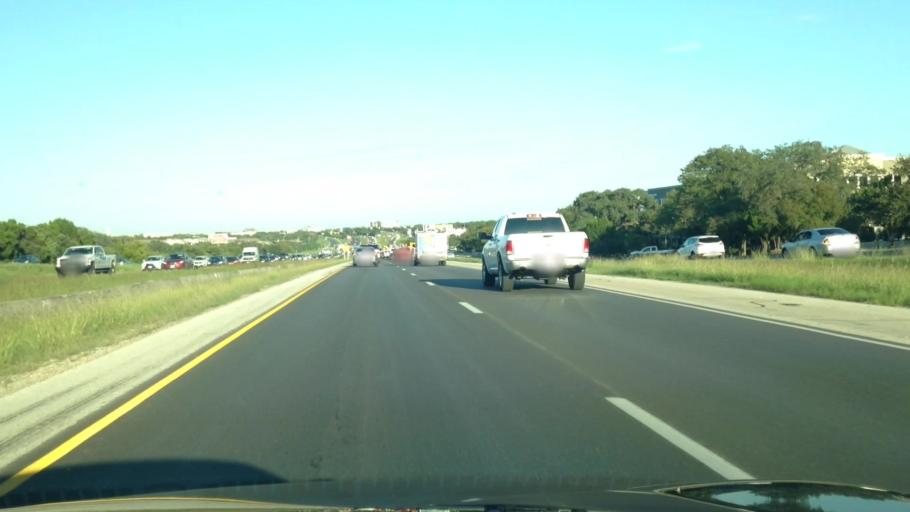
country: US
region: Texas
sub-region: Bexar County
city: Shavano Park
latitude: 29.6019
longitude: -98.5521
